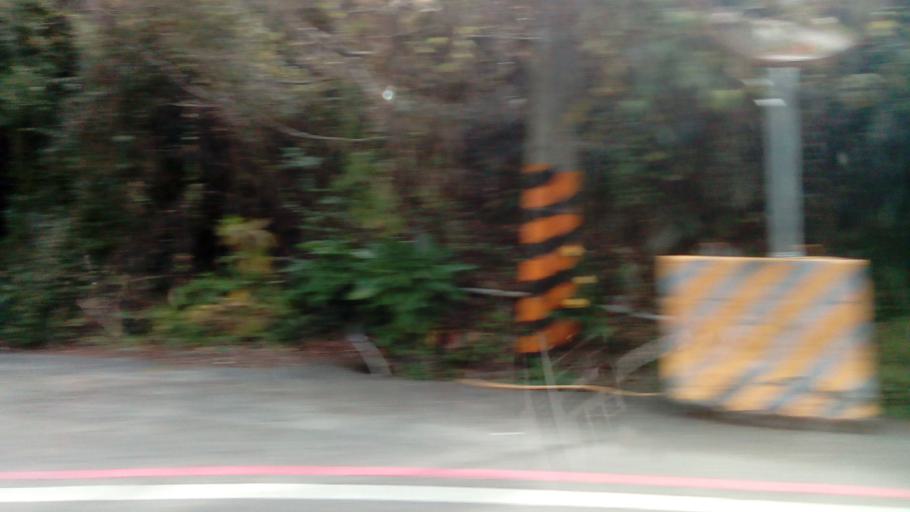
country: TW
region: Taiwan
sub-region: Hualien
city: Hualian
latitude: 24.3561
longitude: 121.3258
